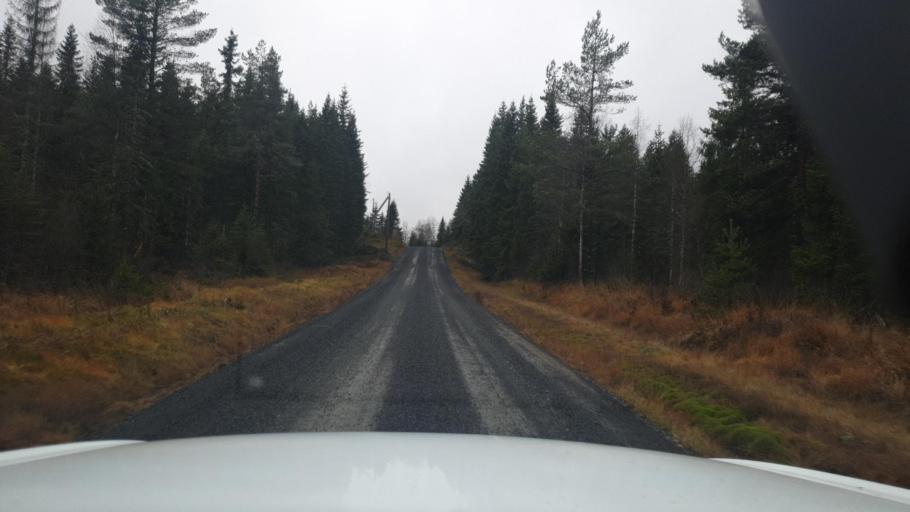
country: SE
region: Vaermland
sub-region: Torsby Kommun
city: Torsby
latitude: 60.1714
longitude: 12.6292
